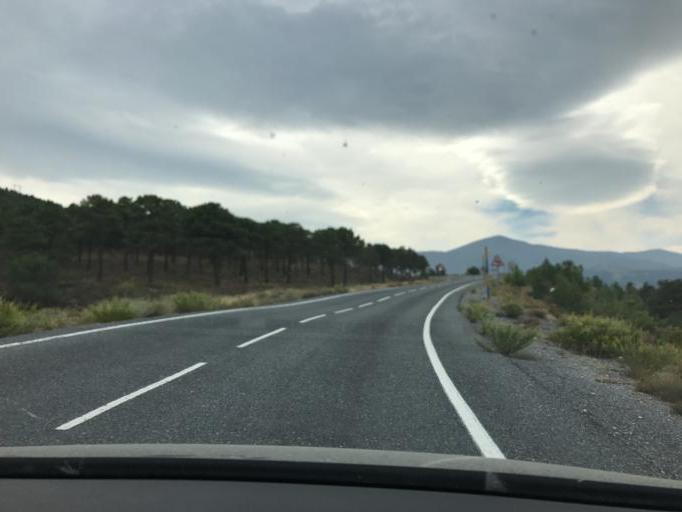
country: ES
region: Andalusia
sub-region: Provincia de Granada
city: Aldeire
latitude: 37.1468
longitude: -3.0488
